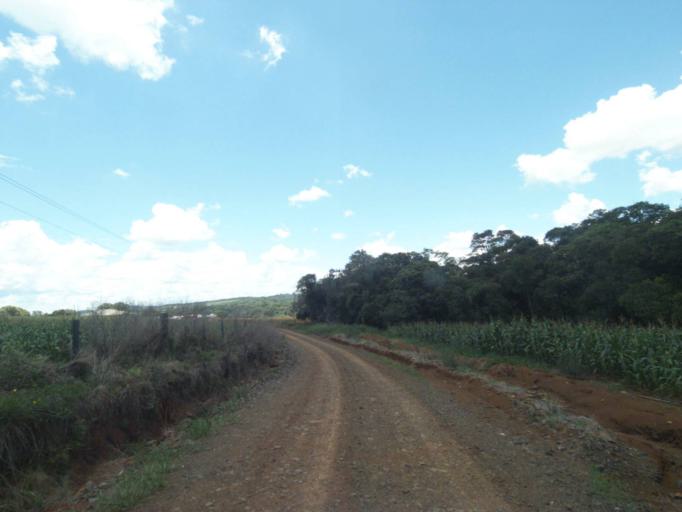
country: BR
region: Parana
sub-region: Pinhao
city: Pinhao
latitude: -25.7886
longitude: -52.0762
